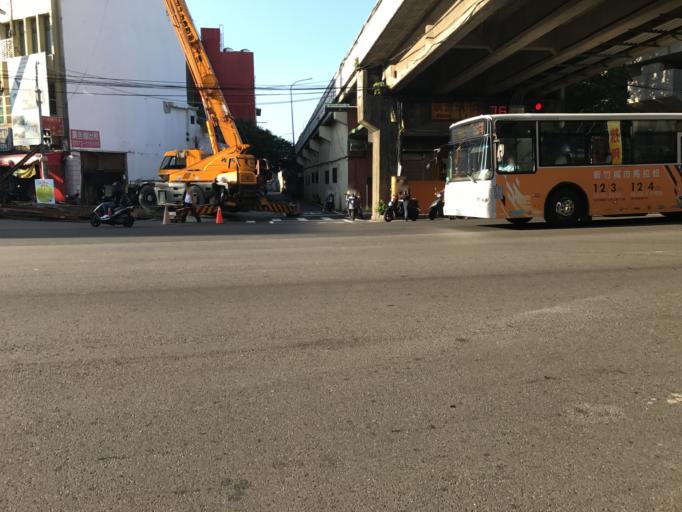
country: TW
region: Taiwan
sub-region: Hsinchu
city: Hsinchu
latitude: 24.8040
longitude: 120.9749
